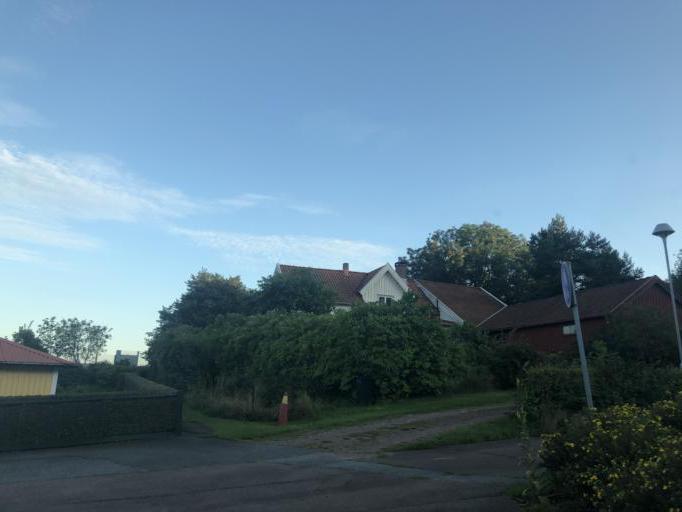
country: SE
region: Vaestra Goetaland
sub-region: Goteborg
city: Goeteborg
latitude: 57.7276
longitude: 11.9790
